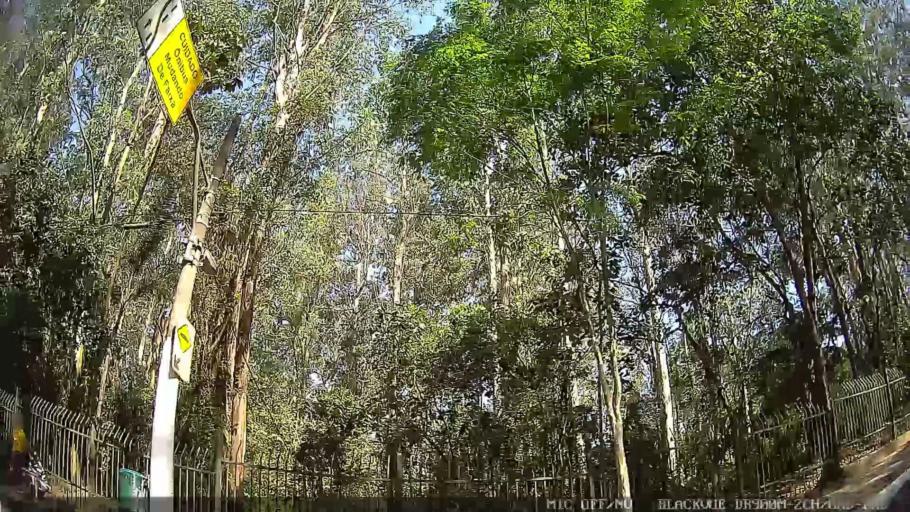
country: BR
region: Sao Paulo
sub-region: Sao Caetano Do Sul
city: Sao Caetano do Sul
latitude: -23.5708
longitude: -46.4696
